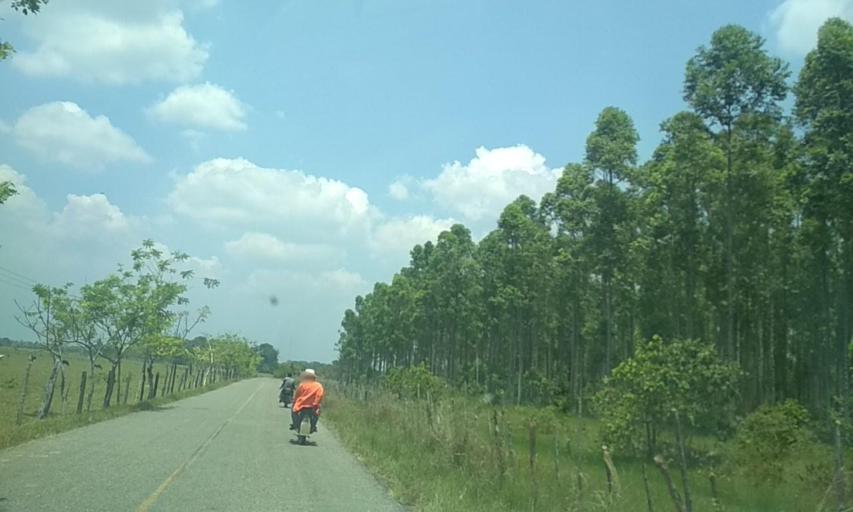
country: MX
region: Tabasco
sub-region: Huimanguillo
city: Francisco Rueda
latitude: 17.8402
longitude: -93.9023
